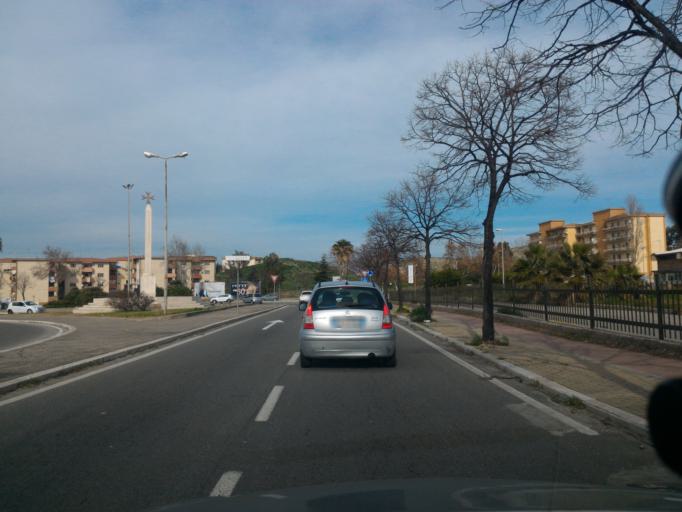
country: IT
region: Calabria
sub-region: Provincia di Crotone
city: Crotone
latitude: 39.0729
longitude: 17.1131
